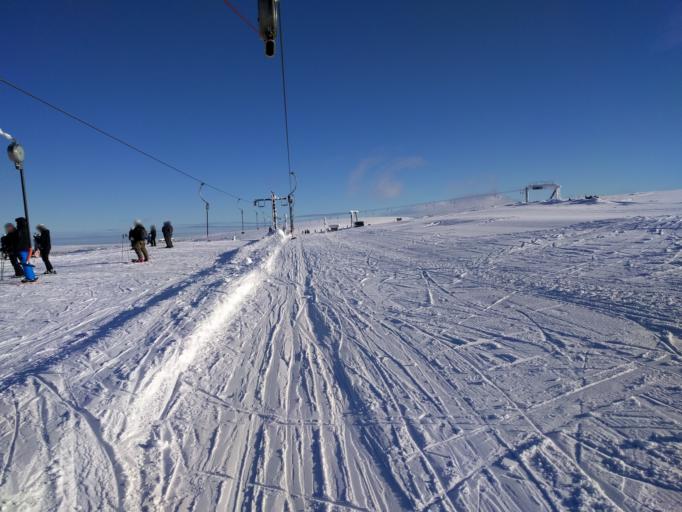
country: NO
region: Hedmark
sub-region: Trysil
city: Innbygda
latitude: 61.1738
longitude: 13.0227
